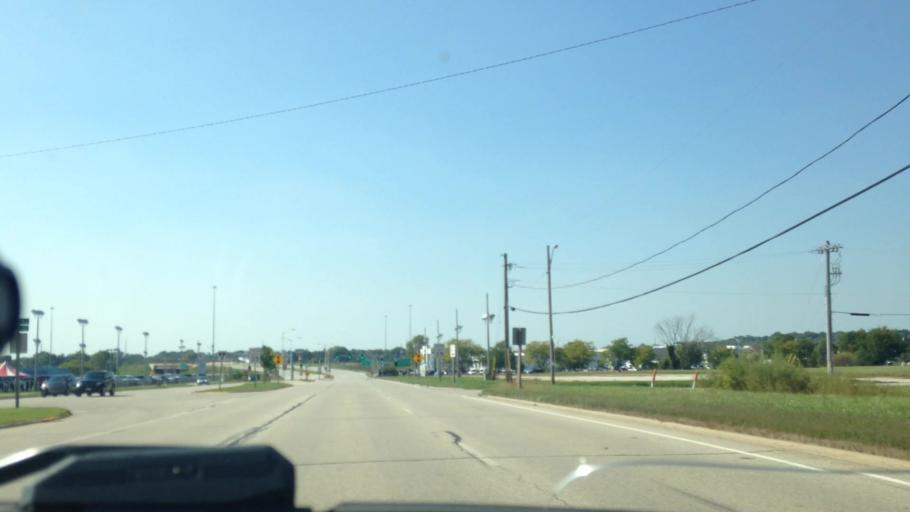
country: US
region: Wisconsin
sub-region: Waukesha County
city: Menomonee Falls
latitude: 43.1779
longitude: -88.0831
